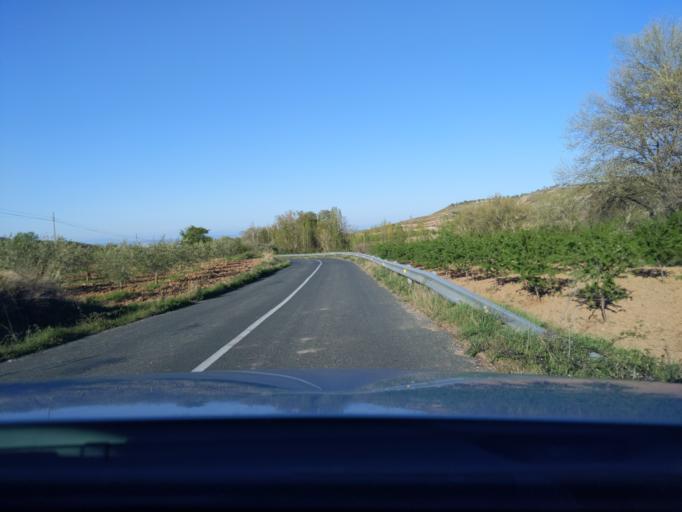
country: ES
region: La Rioja
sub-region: Provincia de La Rioja
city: Bergasa
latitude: 42.2568
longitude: -2.1152
